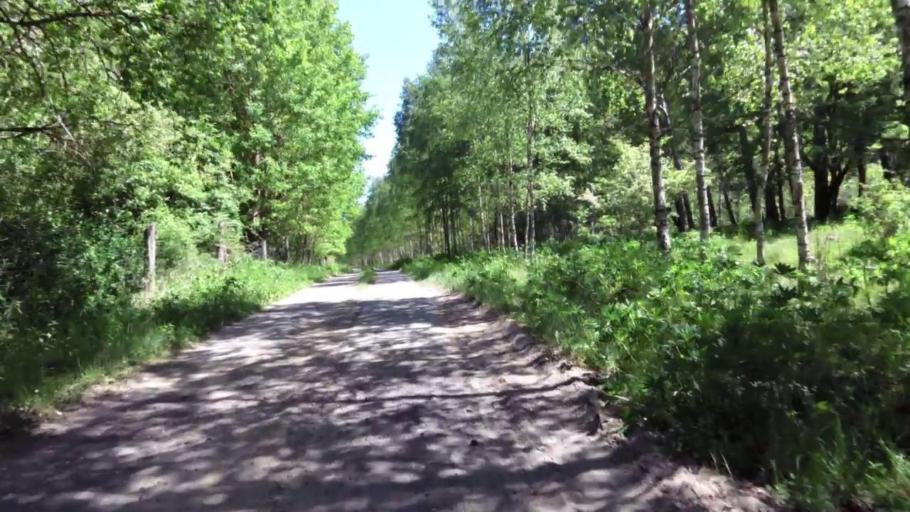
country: PL
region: West Pomeranian Voivodeship
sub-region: Powiat szczecinecki
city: Borne Sulinowo
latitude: 53.5640
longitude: 16.6201
